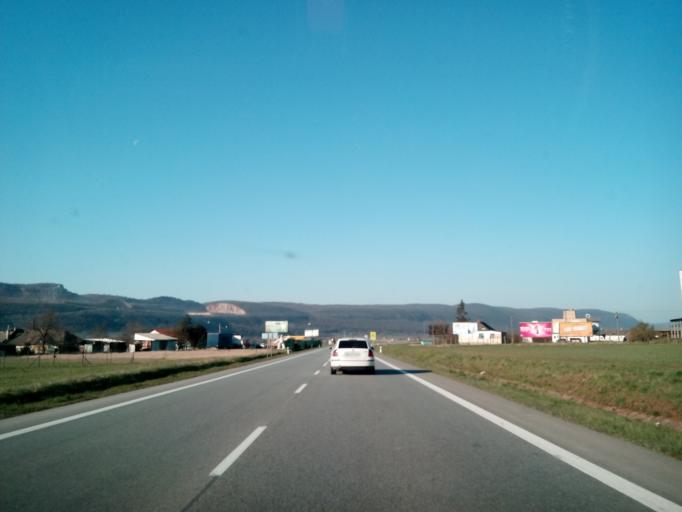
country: SK
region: Kosicky
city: Medzev
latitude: 48.6036
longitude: 20.8338
